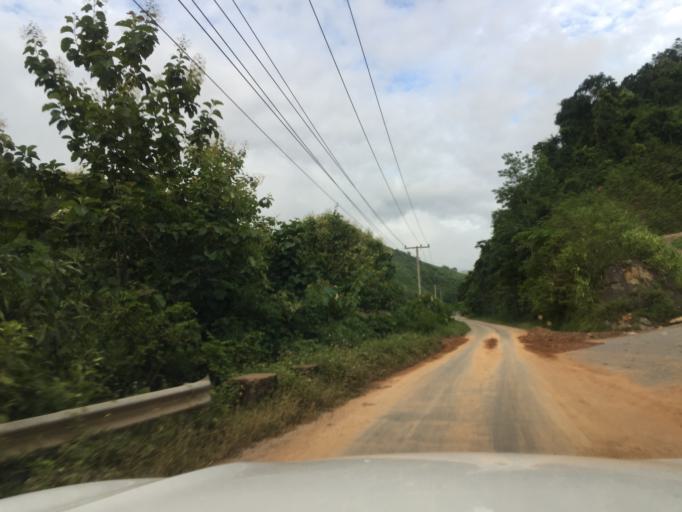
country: LA
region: Phongsali
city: Khoa
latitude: 21.1042
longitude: 102.2976
